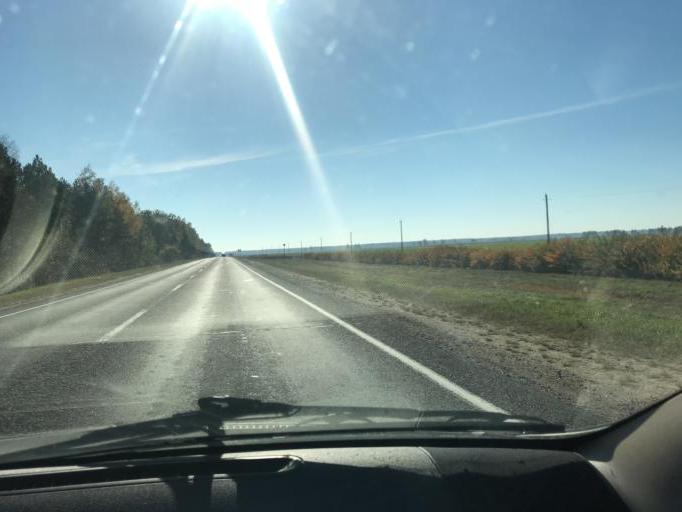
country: BY
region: Minsk
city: Starobin
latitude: 52.5382
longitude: 27.4736
